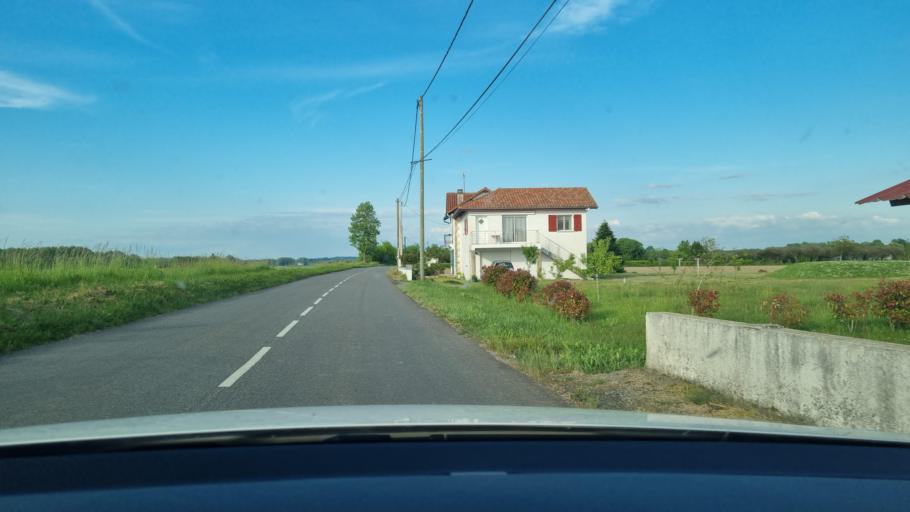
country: FR
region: Aquitaine
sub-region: Departement des Pyrenees-Atlantiques
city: Bardos
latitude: 43.5281
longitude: -1.2211
